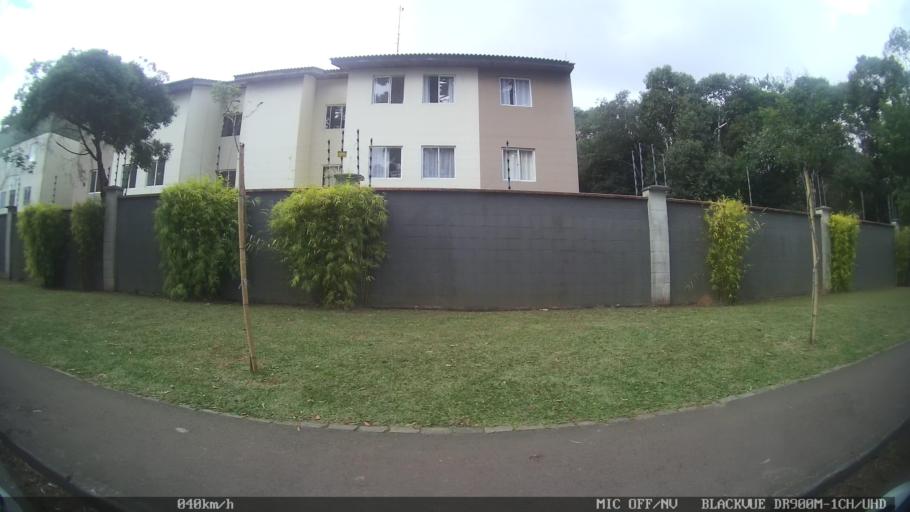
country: BR
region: Parana
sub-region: Colombo
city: Colombo
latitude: -25.3573
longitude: -49.2401
